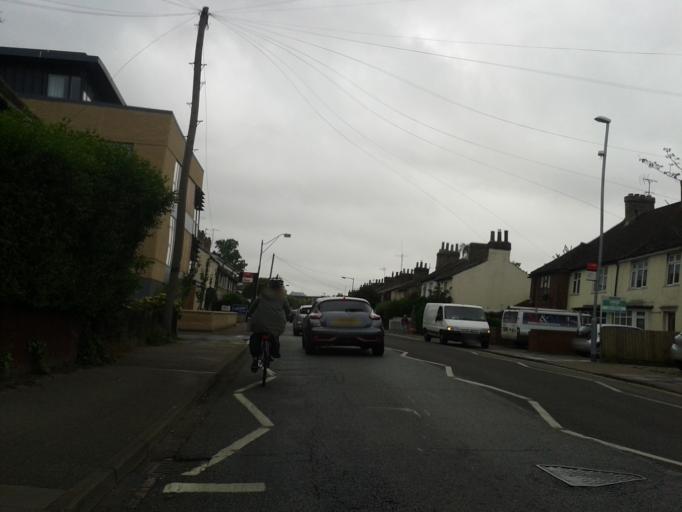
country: GB
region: England
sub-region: Cambridgeshire
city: Cambridge
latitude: 52.2178
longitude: 0.1112
